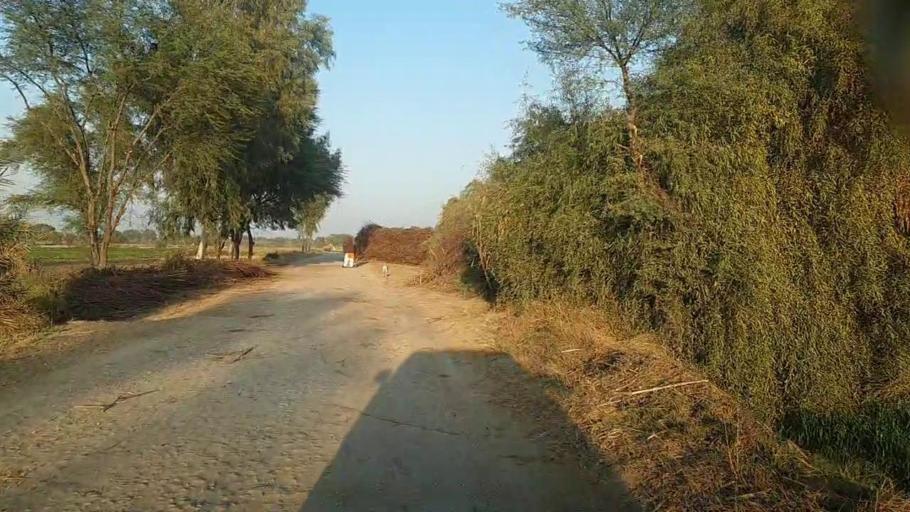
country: PK
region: Sindh
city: Mirpur Mathelo
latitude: 27.8893
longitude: 69.6562
